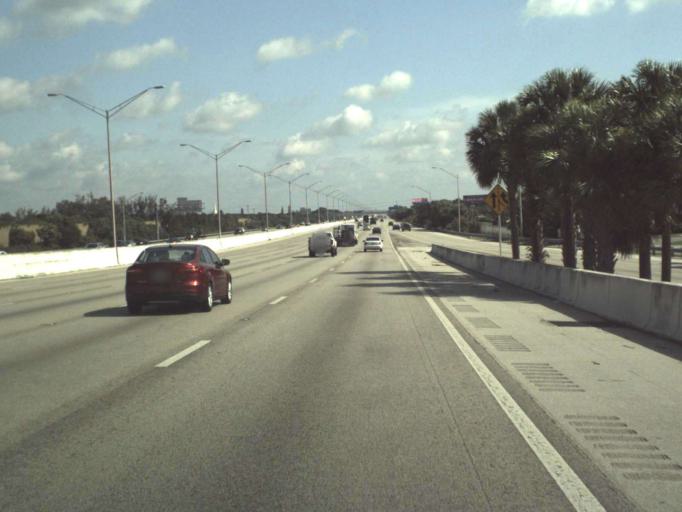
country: US
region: Florida
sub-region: Palm Beach County
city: Lake Park
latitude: 26.7858
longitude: -80.0988
